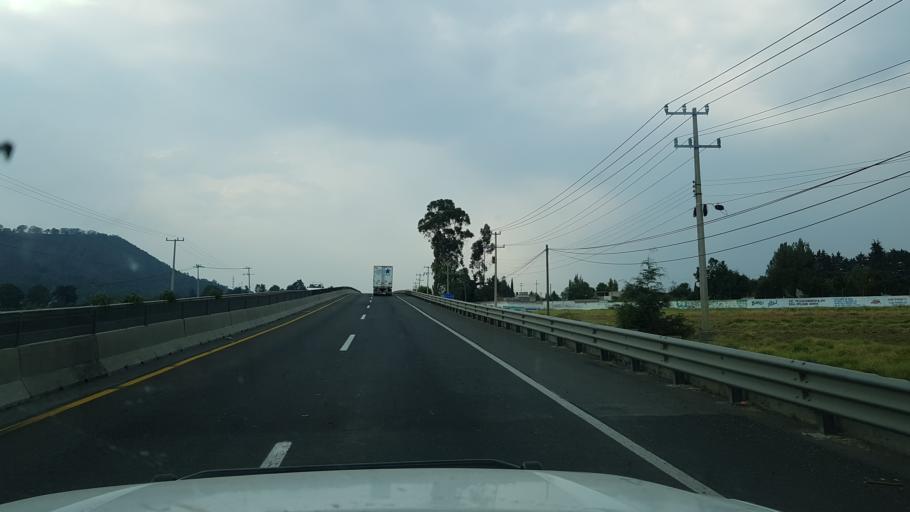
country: MX
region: Mexico
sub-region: Tlalmanalco
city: Santo Tomas Atzingo
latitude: 19.1648
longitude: -98.7818
